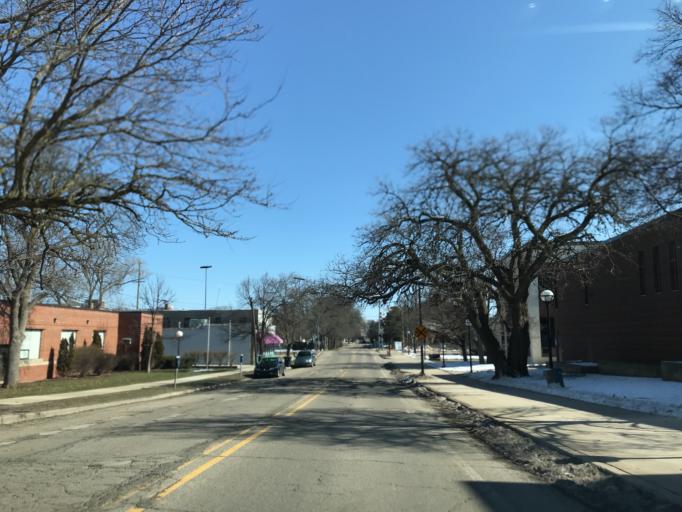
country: US
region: Michigan
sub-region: Washtenaw County
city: Ann Arbor
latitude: 42.2695
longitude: -83.7472
